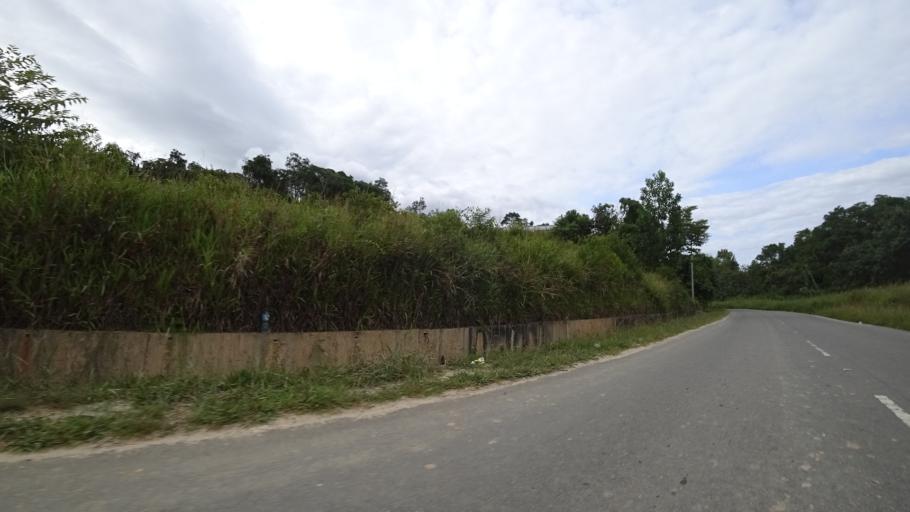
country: BN
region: Brunei and Muara
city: Bandar Seri Begawan
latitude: 4.8518
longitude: 114.9542
